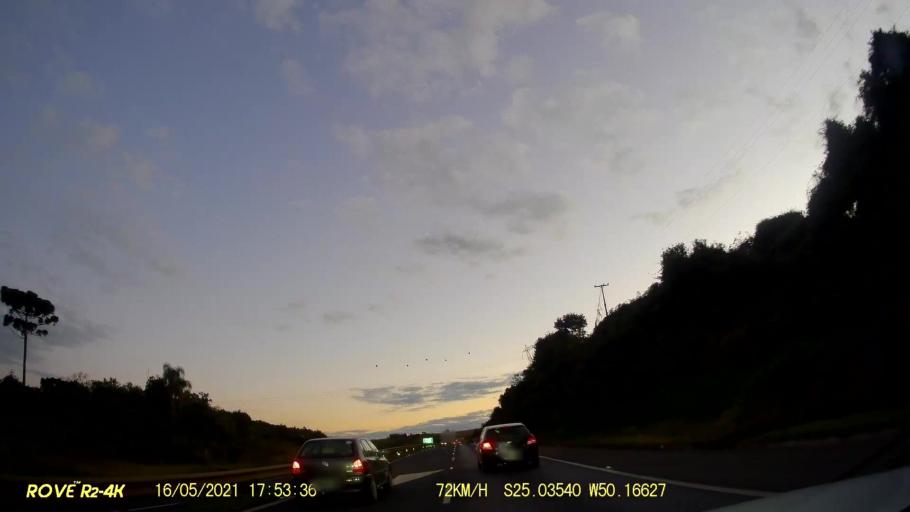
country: BR
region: Parana
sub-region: Ponta Grossa
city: Ponta Grossa
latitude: -25.0355
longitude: -50.1663
